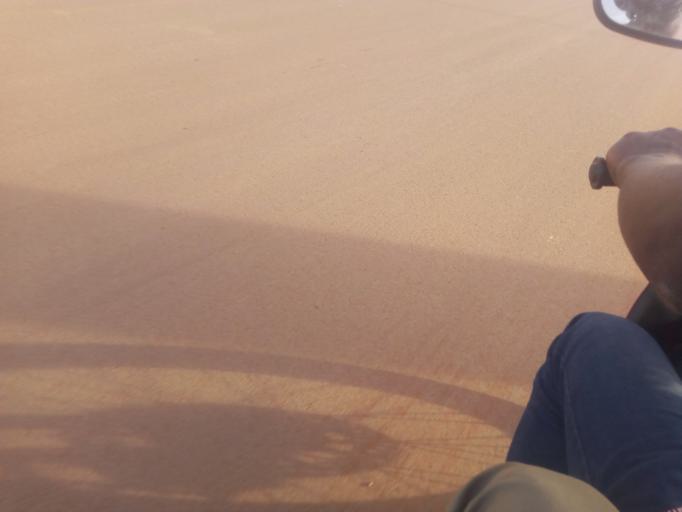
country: BF
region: Centre
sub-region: Kadiogo Province
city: Ouagadougou
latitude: 12.3961
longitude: -1.5562
